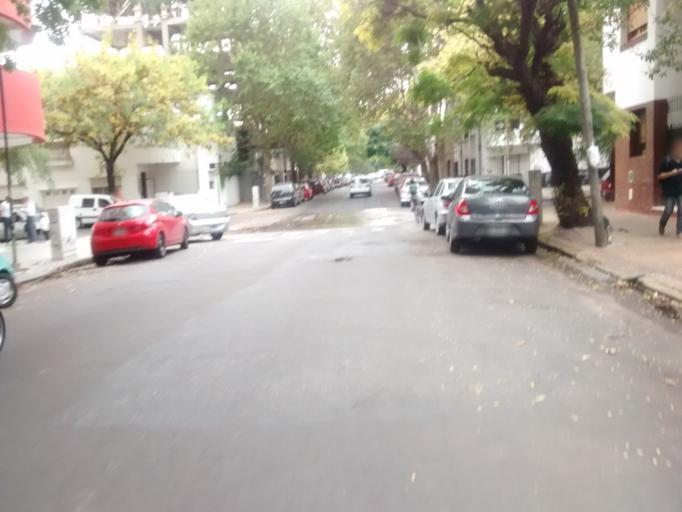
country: AR
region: Buenos Aires
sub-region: Partido de La Plata
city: La Plata
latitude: -34.9263
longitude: -57.9503
